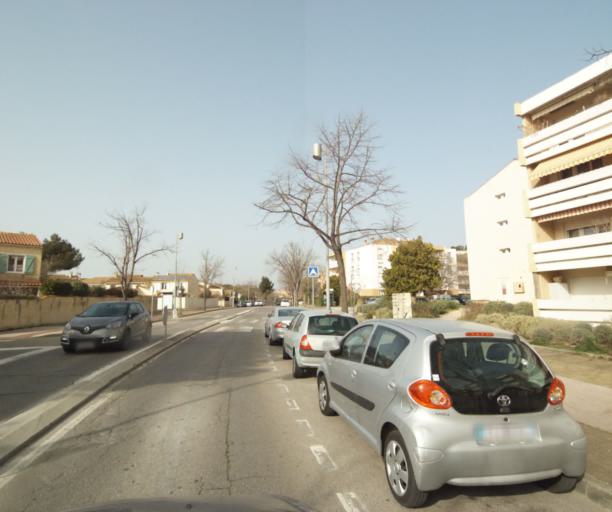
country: FR
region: Provence-Alpes-Cote d'Azur
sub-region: Departement des Bouches-du-Rhone
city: Vitrolles
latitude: 43.4595
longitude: 5.2424
